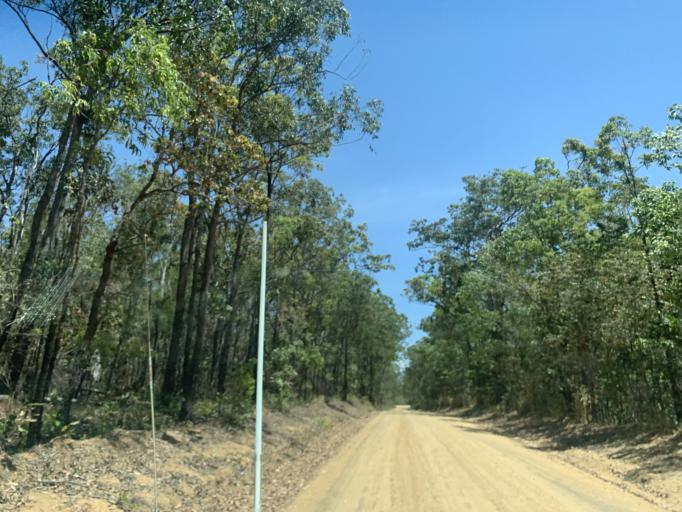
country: AU
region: Queensland
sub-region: Tablelands
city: Kuranda
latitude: -16.9199
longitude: 145.5911
